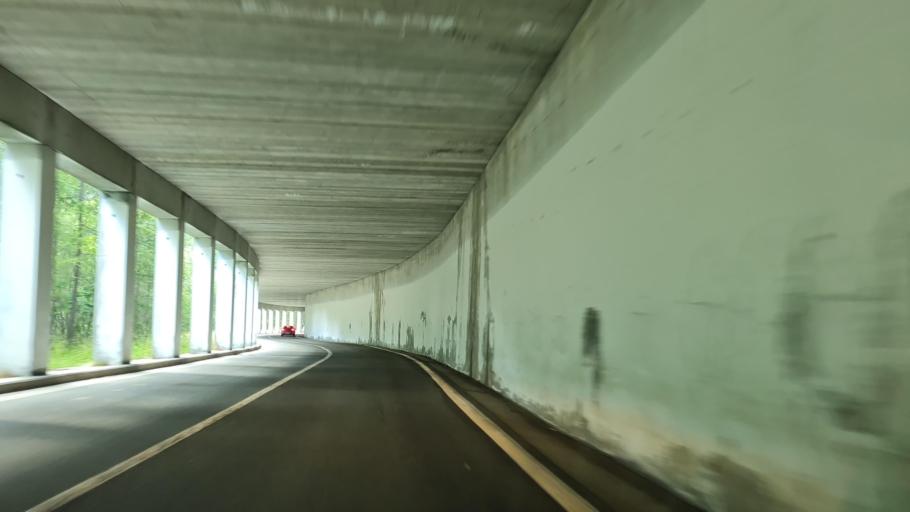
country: IT
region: Piedmont
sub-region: Provincia Verbano-Cusio-Ossola
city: Formazza
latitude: 46.4048
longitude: 8.4176
